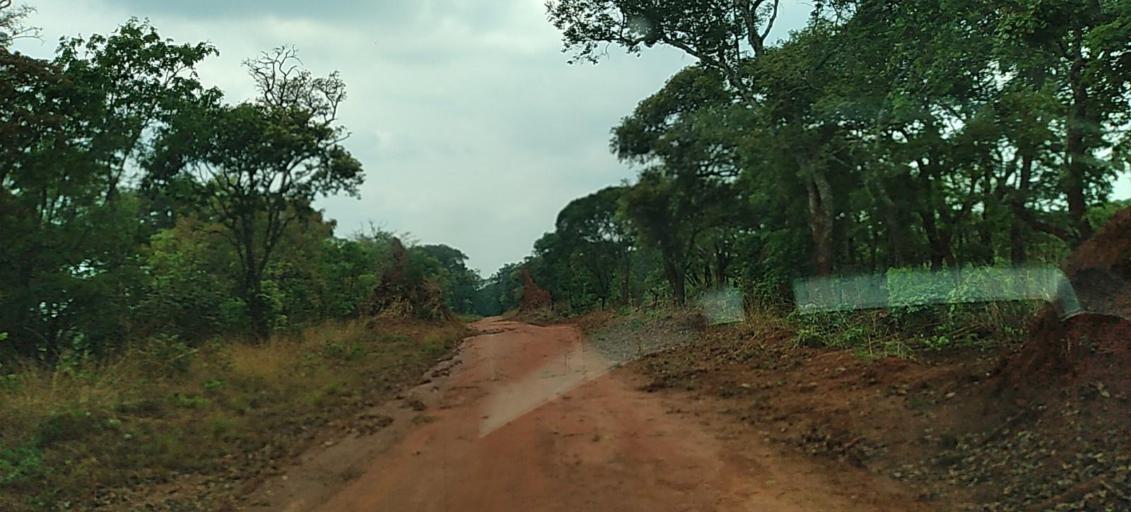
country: ZM
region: North-Western
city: Mwinilunga
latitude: -11.5440
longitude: 24.7789
